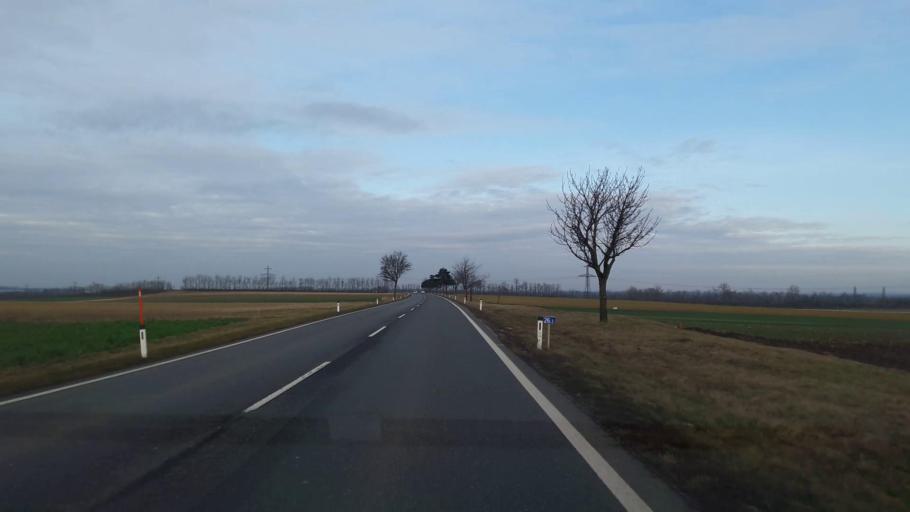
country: AT
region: Lower Austria
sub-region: Politischer Bezirk Mistelbach
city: Staatz
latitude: 48.6989
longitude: 16.4419
